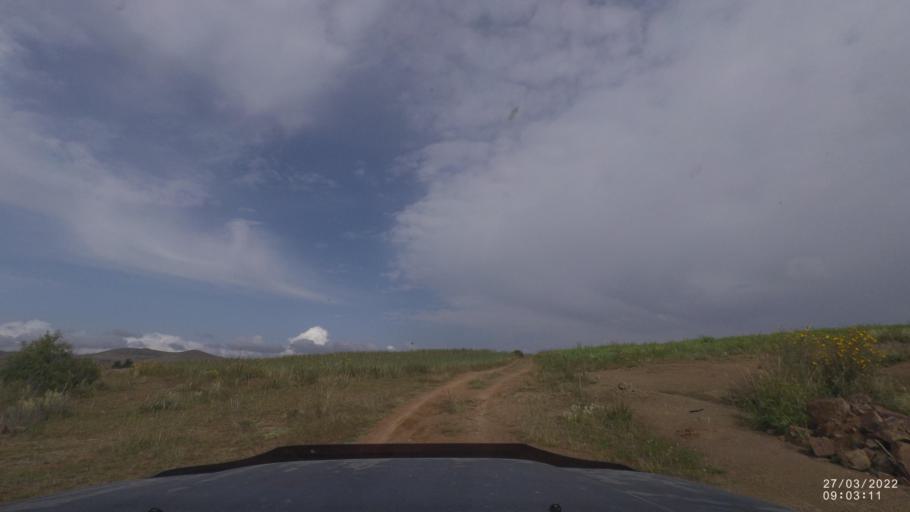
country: BO
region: Cochabamba
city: Cliza
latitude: -17.7367
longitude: -65.8599
